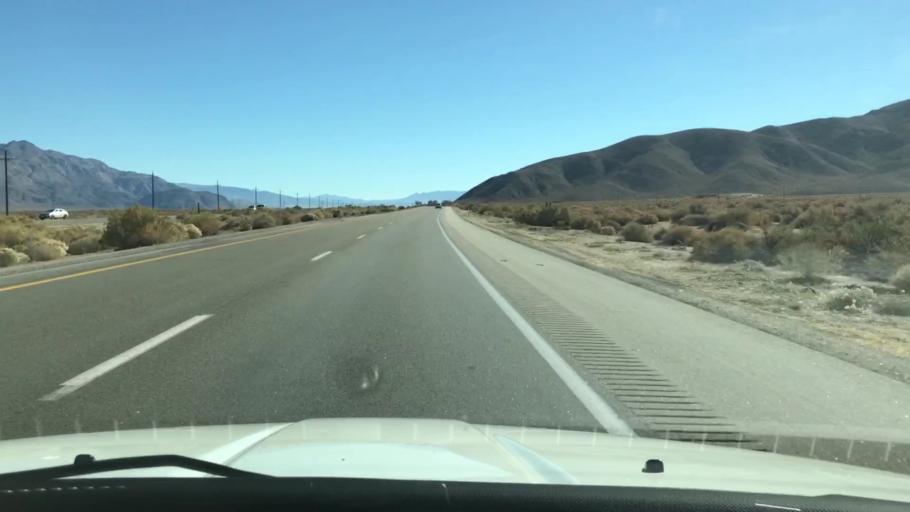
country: US
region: California
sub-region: Inyo County
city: Lone Pine
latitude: 36.6912
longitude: -118.1133
